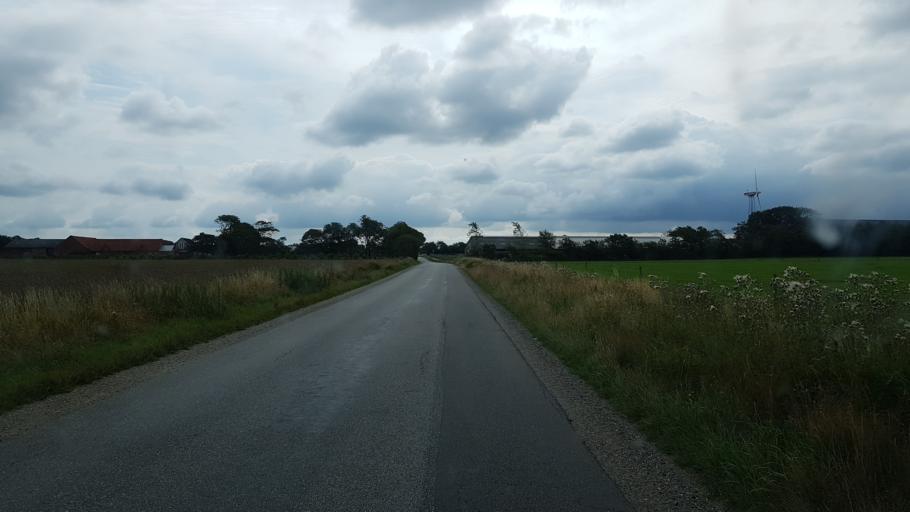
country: DK
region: South Denmark
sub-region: Varde Kommune
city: Varde
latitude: 55.7294
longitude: 8.5196
